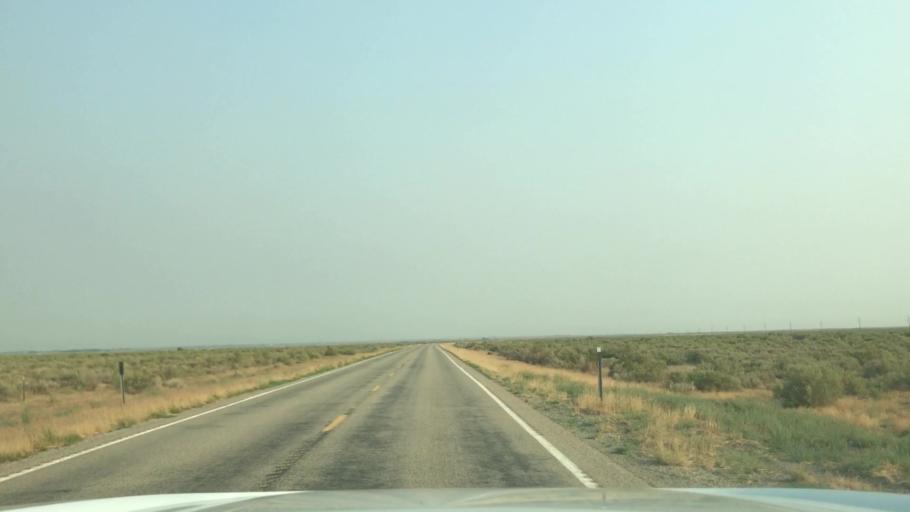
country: US
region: Utah
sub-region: Millard County
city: Delta
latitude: 39.2624
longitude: -112.4480
